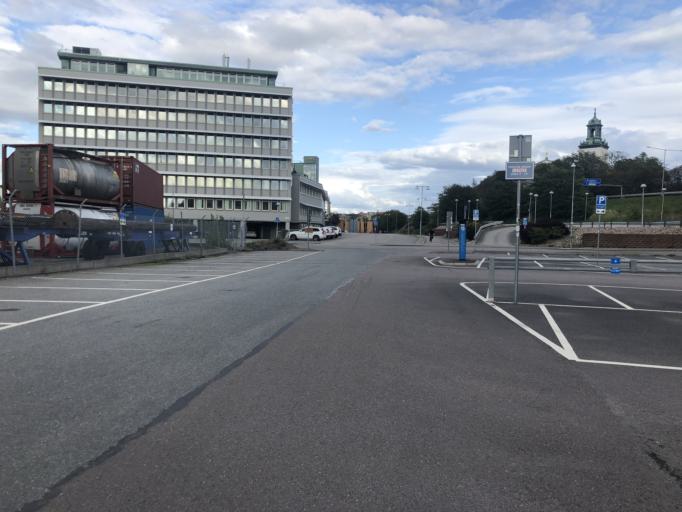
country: SE
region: Vaestra Goetaland
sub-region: Goteborg
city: Majorna
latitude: 57.6962
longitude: 11.9189
